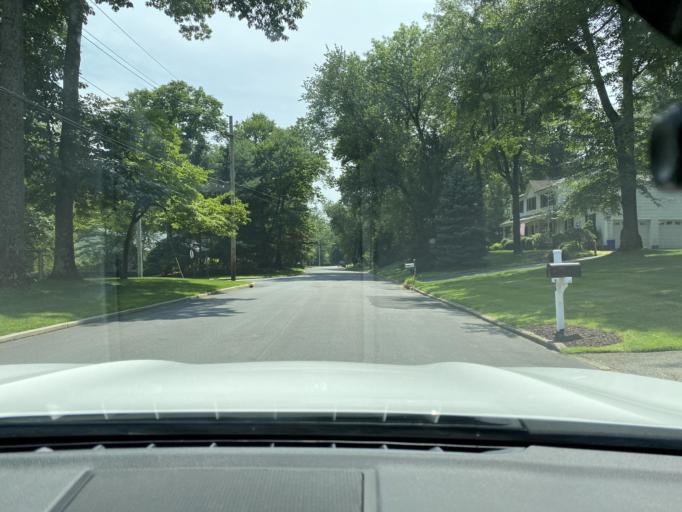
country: US
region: New York
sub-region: Rockland County
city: Airmont
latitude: 41.0807
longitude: -74.1073
